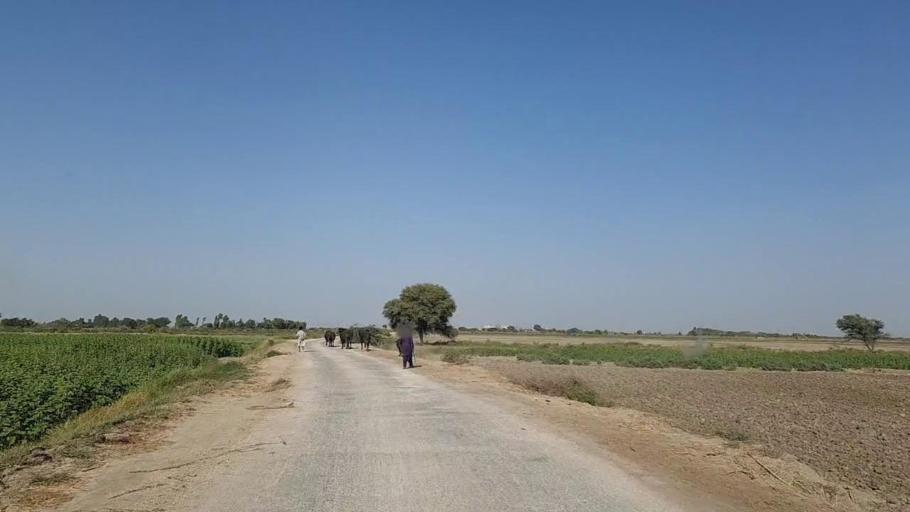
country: PK
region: Sindh
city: Chuhar Jamali
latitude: 24.5251
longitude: 68.1114
